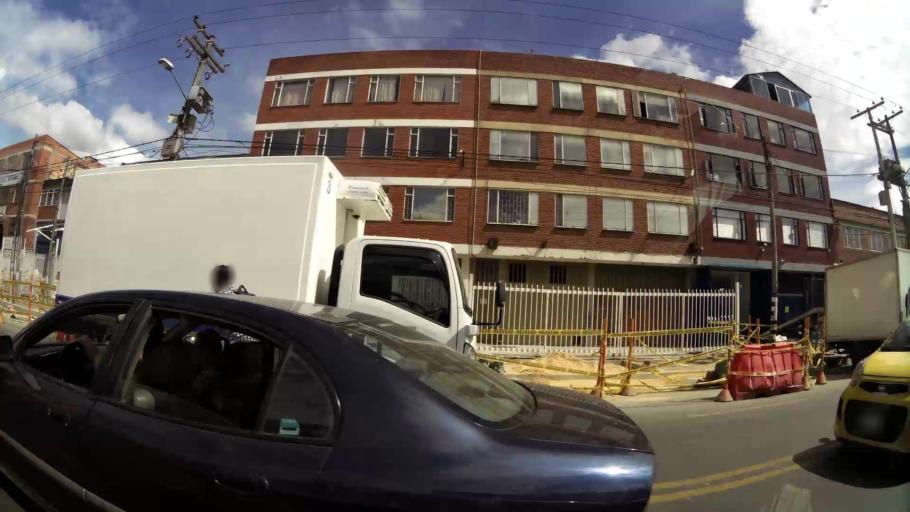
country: CO
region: Bogota D.C.
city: Bogota
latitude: 4.6162
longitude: -74.1314
